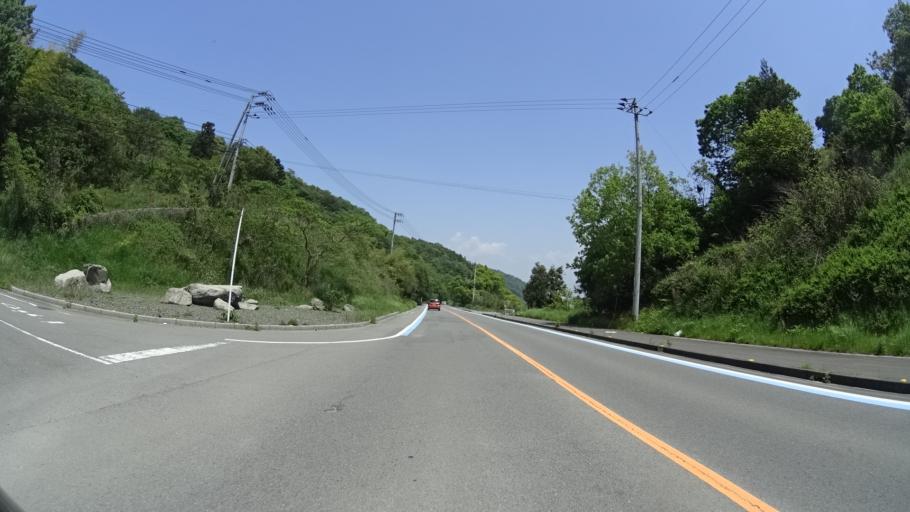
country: JP
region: Ehime
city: Iyo
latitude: 33.7198
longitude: 132.6777
